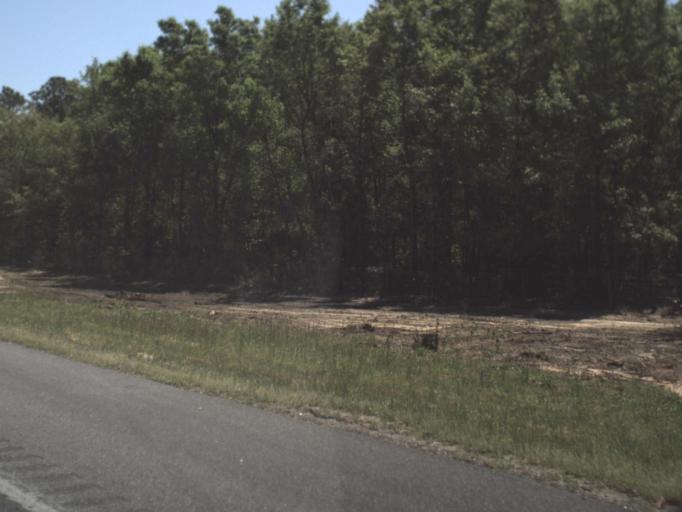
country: US
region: Florida
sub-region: Escambia County
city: Ferry Pass
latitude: 30.5026
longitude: -87.1997
